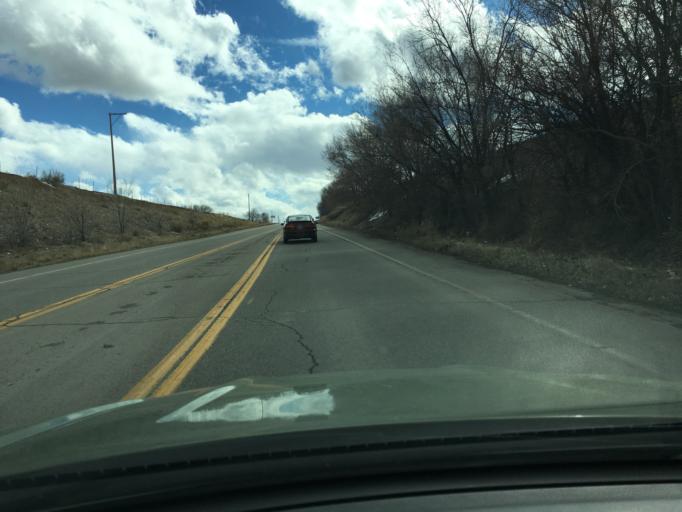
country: US
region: Colorado
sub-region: Mesa County
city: Clifton
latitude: 39.0527
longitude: -108.4596
